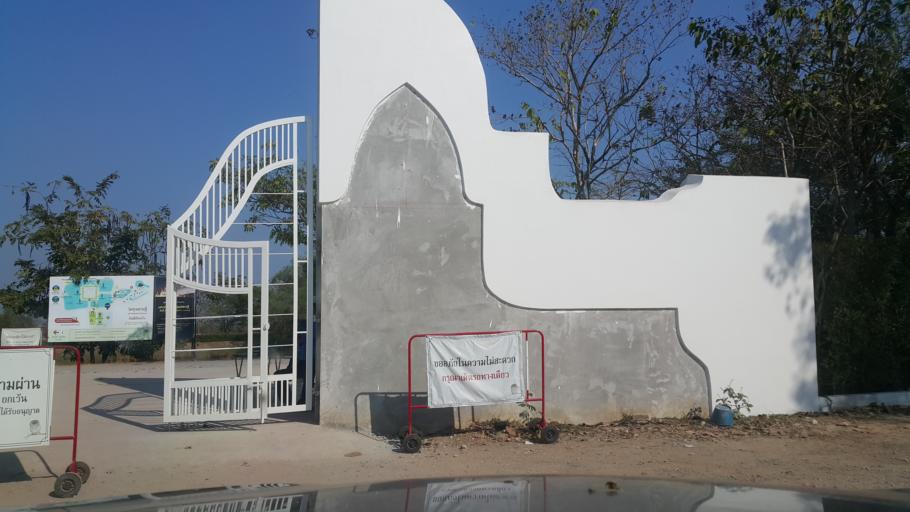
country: TH
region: Khon Kaen
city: Khon Kaen
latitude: 16.4106
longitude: 102.8832
